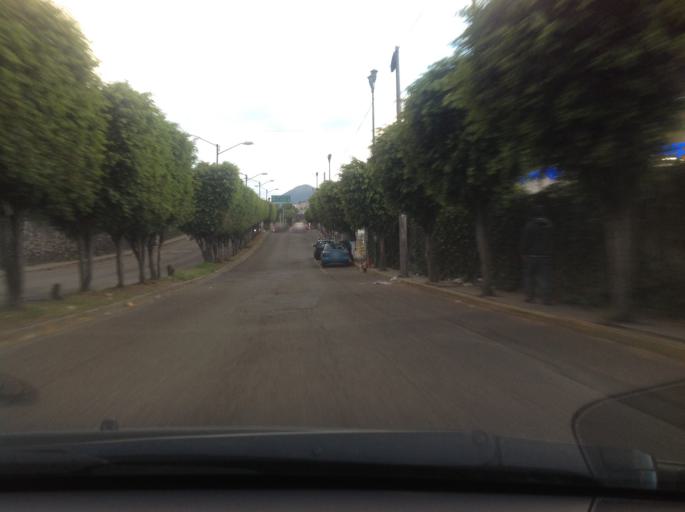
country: MX
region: Mexico City
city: Magdalena Contreras
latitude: 19.3057
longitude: -99.2204
